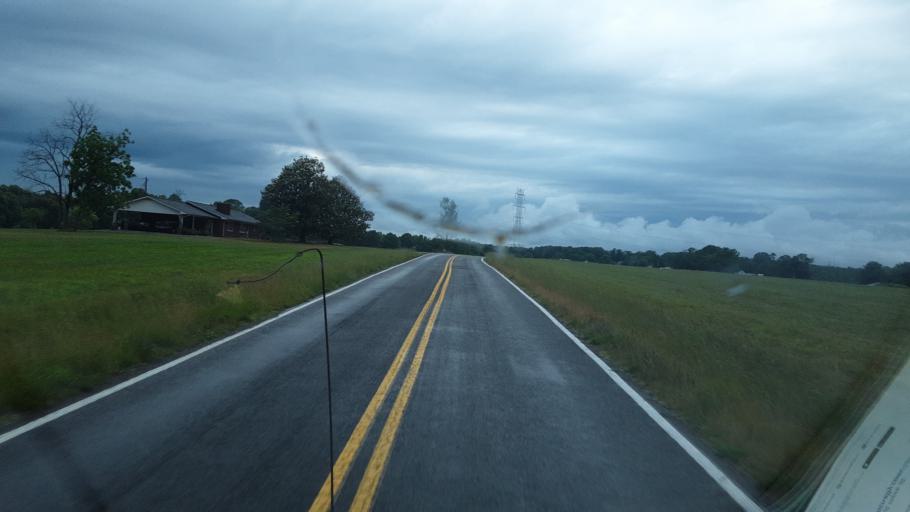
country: US
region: North Carolina
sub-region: Yadkin County
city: Jonesville
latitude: 36.0829
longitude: -80.8447
